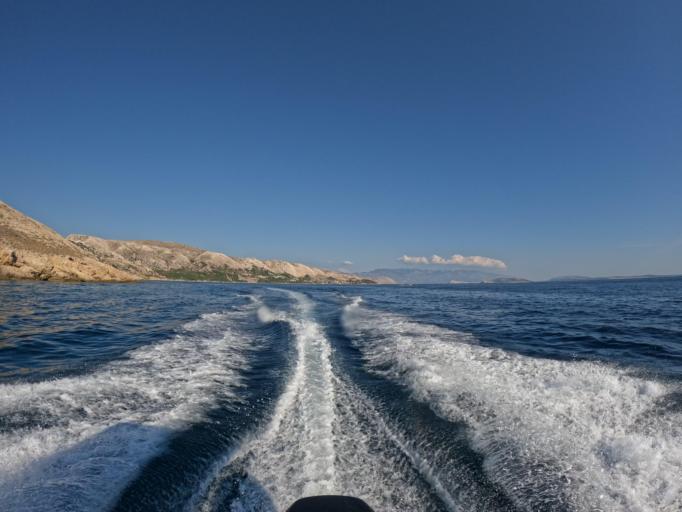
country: HR
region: Primorsko-Goranska
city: Punat
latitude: 44.9633
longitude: 14.6520
